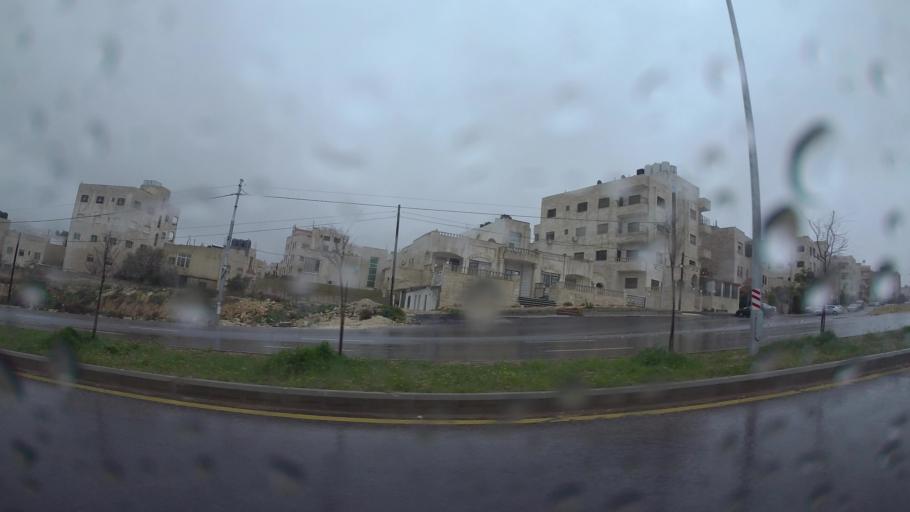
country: JO
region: Amman
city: Al Jubayhah
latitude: 32.0465
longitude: 35.8839
